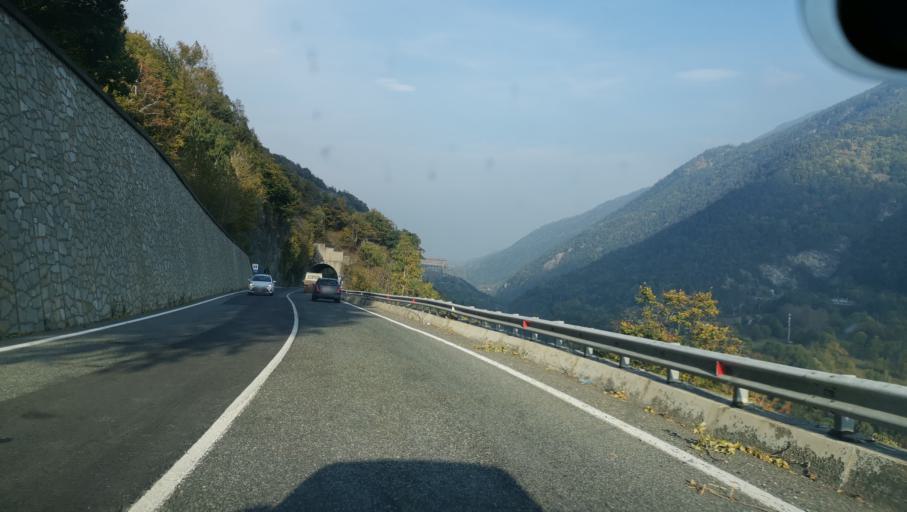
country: IT
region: Piedmont
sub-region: Provincia di Torino
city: Exilles
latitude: 45.0906
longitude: 6.9155
